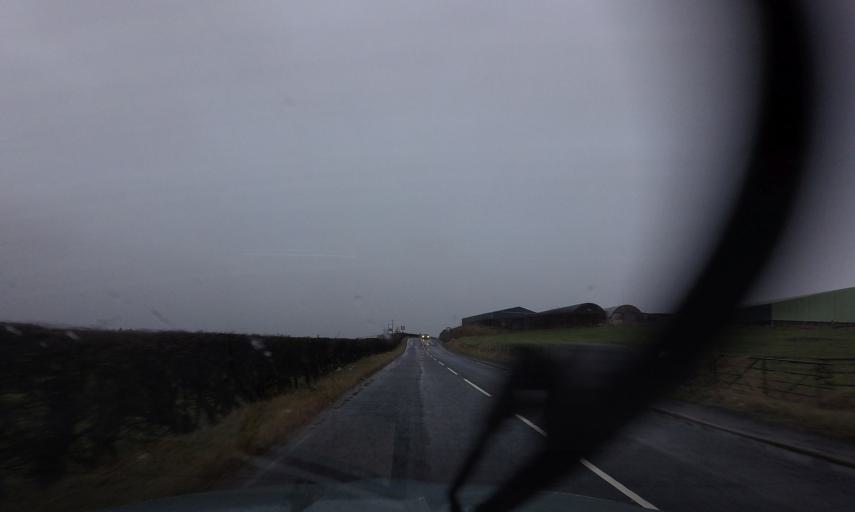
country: GB
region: Scotland
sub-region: North Lanarkshire
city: Shotts
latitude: 55.8112
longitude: -3.8021
